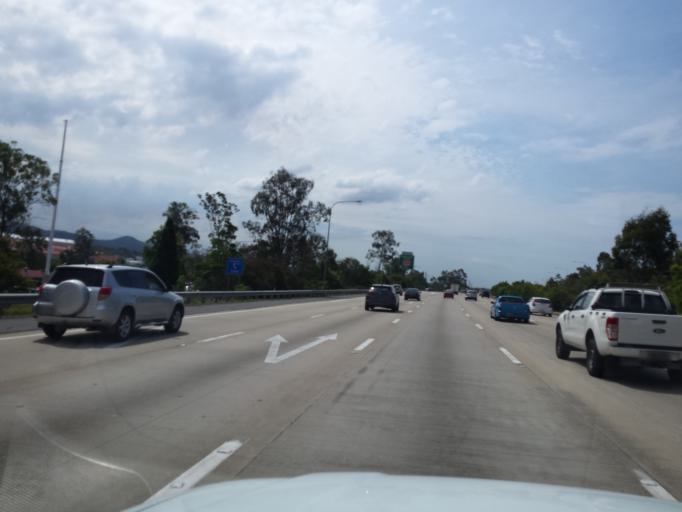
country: AU
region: Queensland
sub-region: Gold Coast
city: Upper Coomera
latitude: -27.9146
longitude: 153.3197
